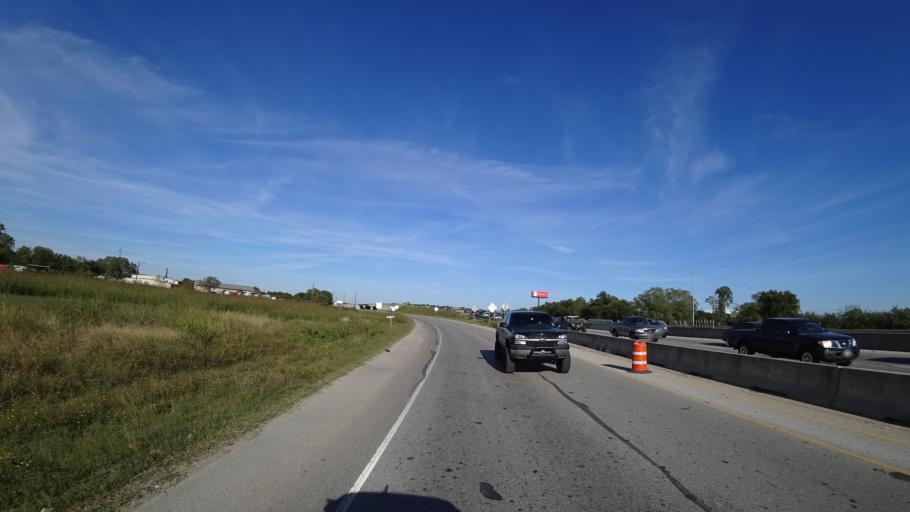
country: US
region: Texas
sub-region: Travis County
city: Austin
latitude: 30.2512
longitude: -97.6834
